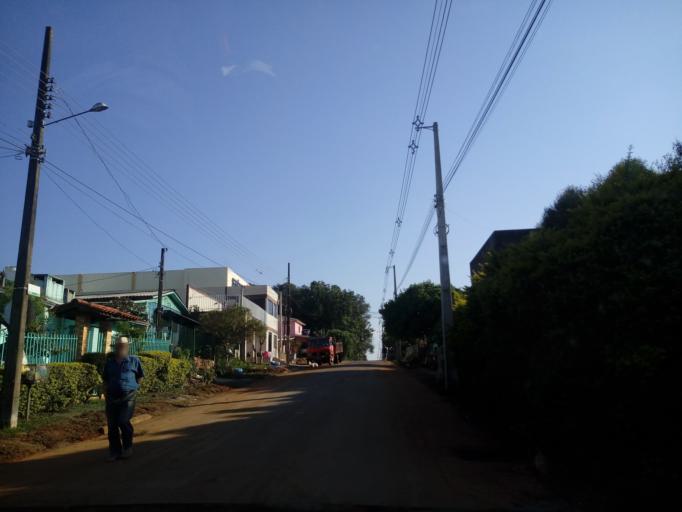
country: BR
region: Santa Catarina
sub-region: Chapeco
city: Chapeco
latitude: -27.0942
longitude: -52.6751
